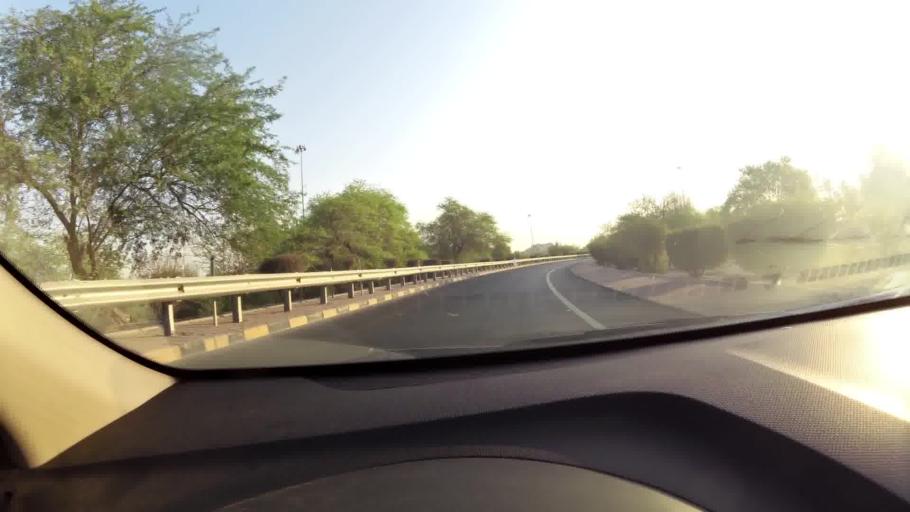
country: KW
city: Bayan
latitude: 29.3059
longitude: 48.0247
